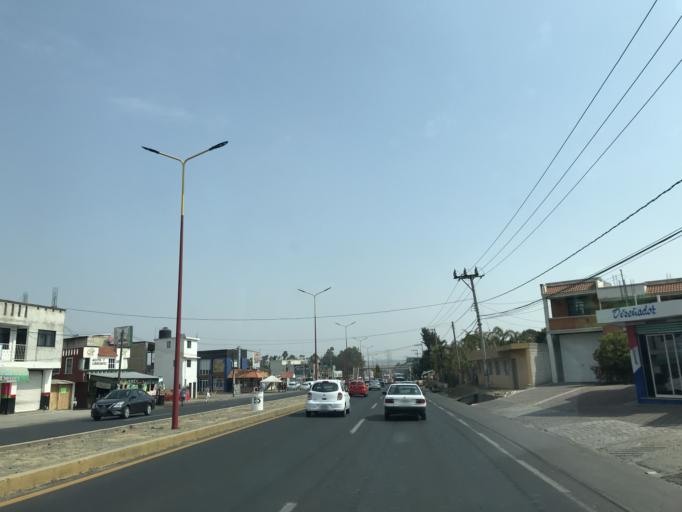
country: MX
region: Tlaxcala
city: La Magdalena Tlaltelulco
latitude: 19.2891
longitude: -98.1951
